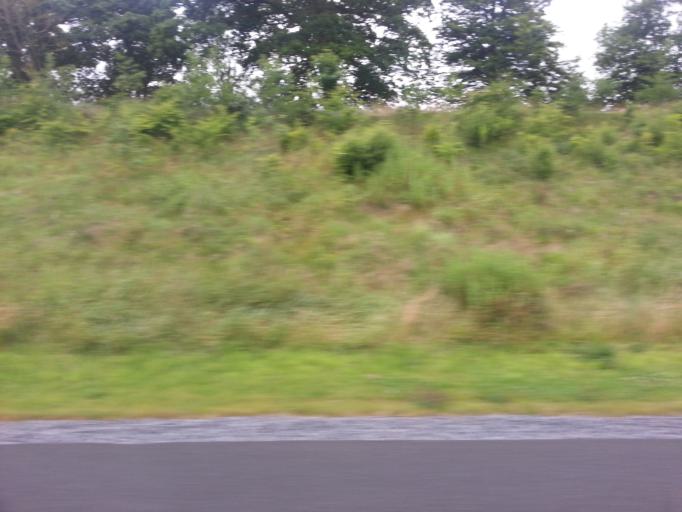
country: IE
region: Leinster
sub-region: Kilkenny
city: Kilkenny
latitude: 52.6475
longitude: -7.1893
